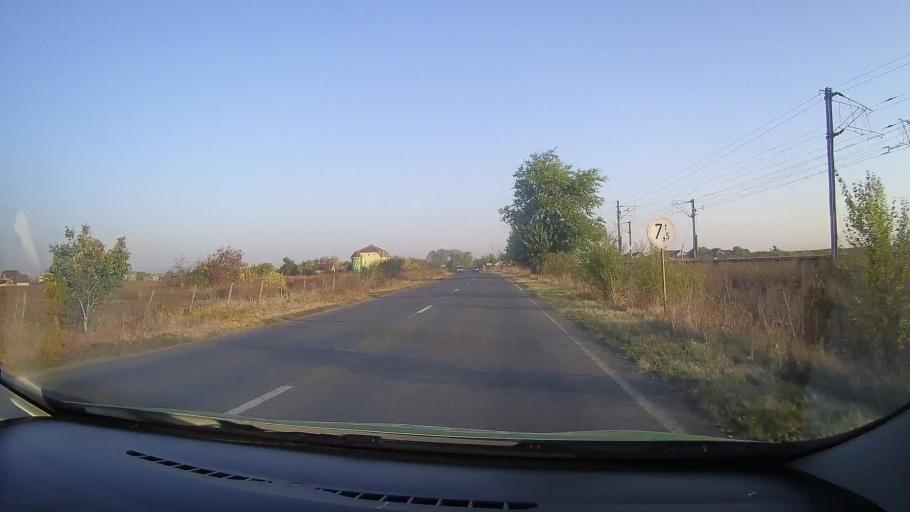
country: RO
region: Arad
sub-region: Comuna Sofronea
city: Sofronea
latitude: 46.2714
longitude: 21.3154
